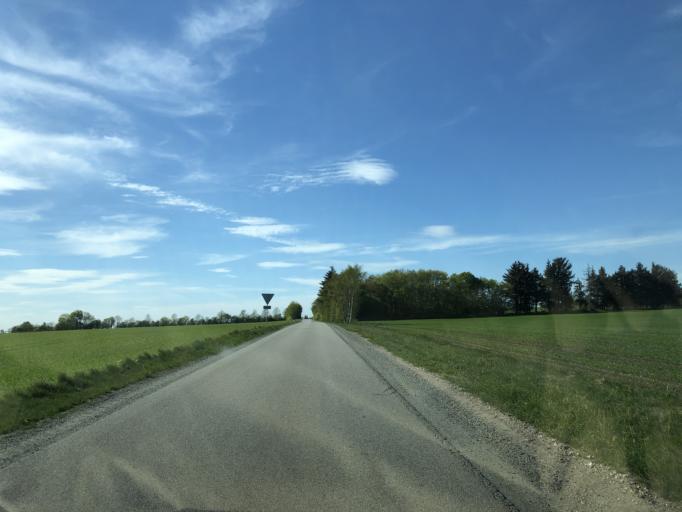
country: DK
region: Central Jutland
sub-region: Ringkobing-Skjern Kommune
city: Videbaek
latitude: 56.1668
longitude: 8.5358
